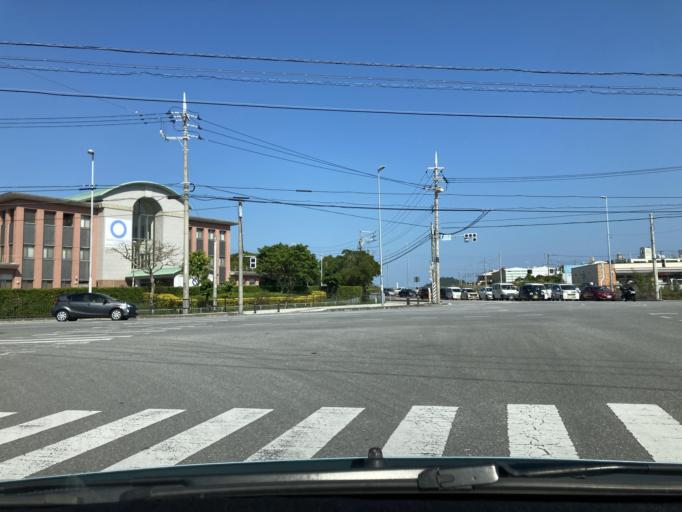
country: JP
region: Okinawa
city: Naha-shi
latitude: 26.2044
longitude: 127.7257
